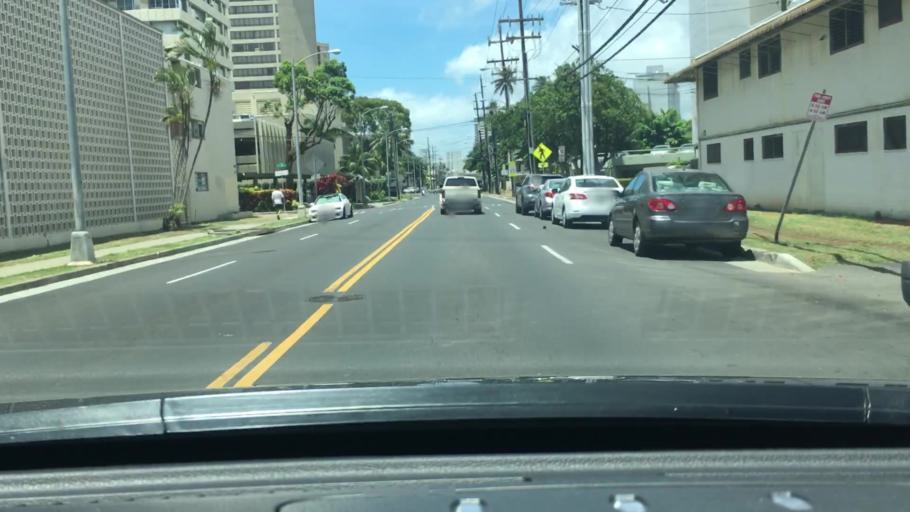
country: US
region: Hawaii
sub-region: Honolulu County
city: Honolulu
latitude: 21.2861
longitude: -157.8220
